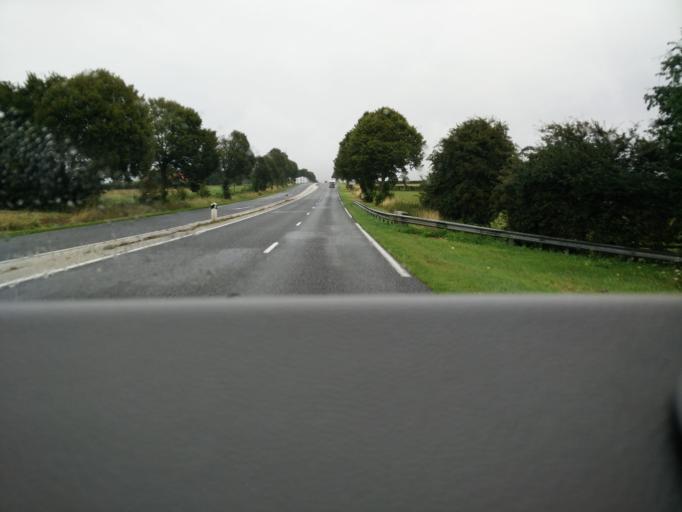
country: FR
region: Nord-Pas-de-Calais
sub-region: Departement du Pas-de-Calais
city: Auchy-les-Hesdin
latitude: 50.3806
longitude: 2.1161
